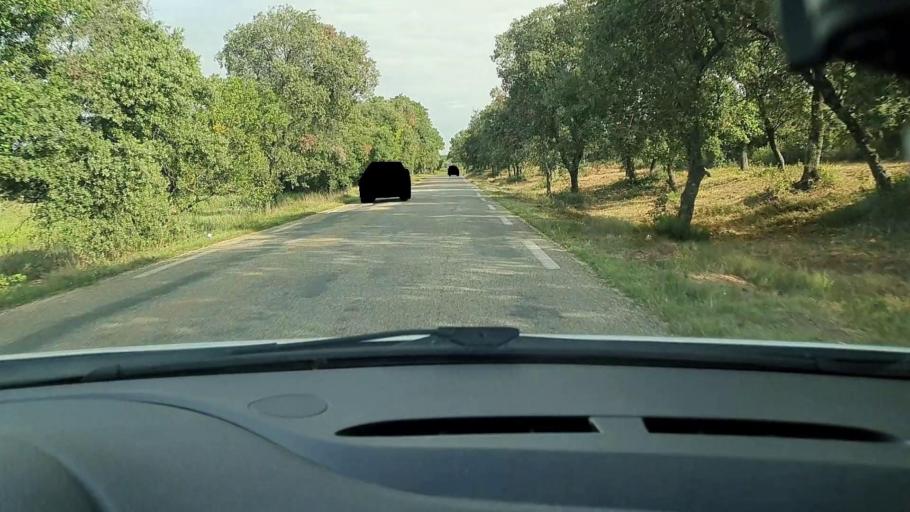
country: FR
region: Languedoc-Roussillon
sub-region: Departement du Gard
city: Saint-Quentin-la-Poterie
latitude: 44.0898
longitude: 4.4546
